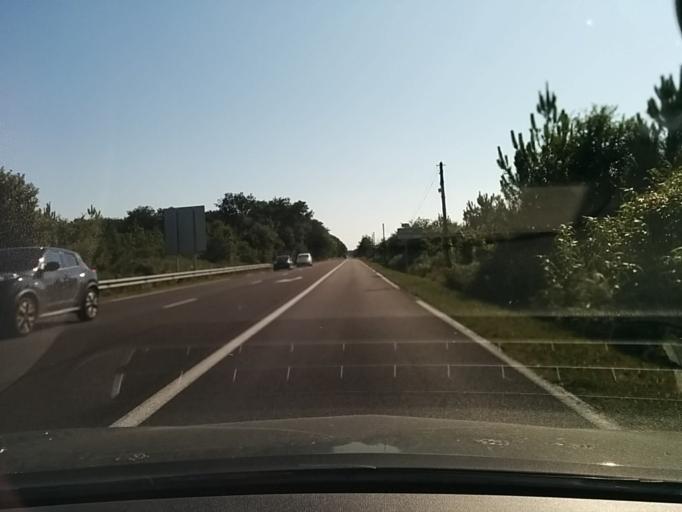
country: FR
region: Aquitaine
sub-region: Departement des Landes
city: Benesse-Maremne
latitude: 43.6262
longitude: -1.3755
